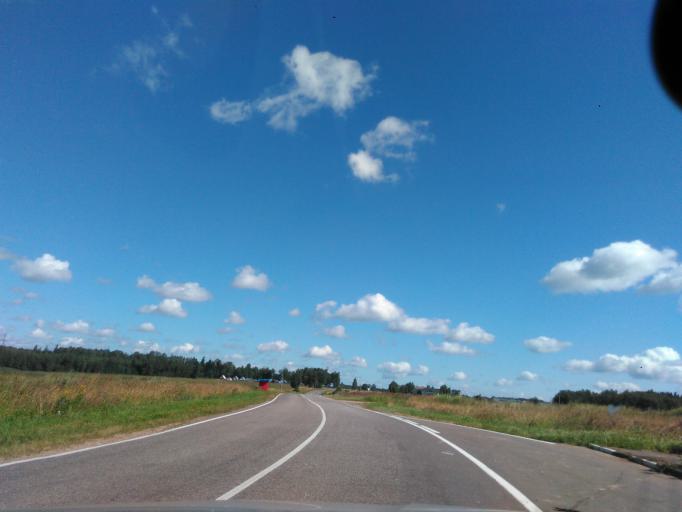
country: RU
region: Moskovskaya
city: Klin
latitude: 56.1839
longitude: 36.8084
